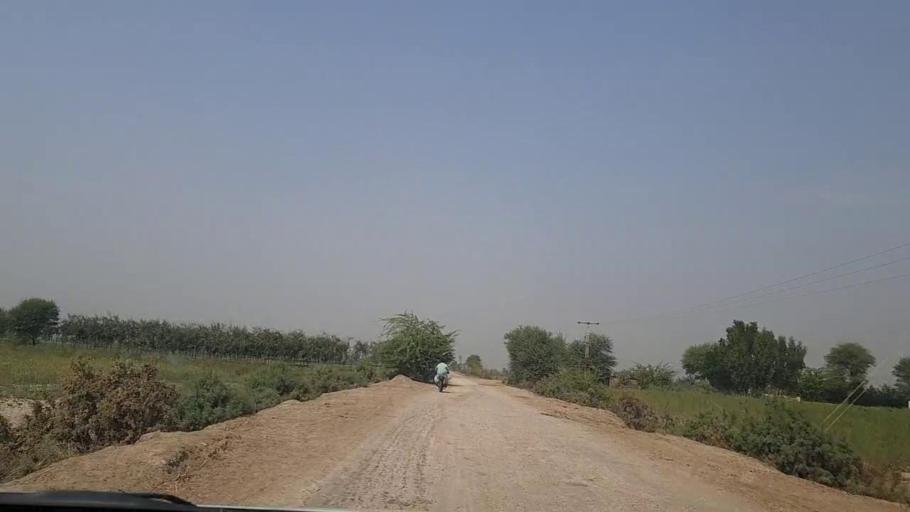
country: PK
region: Sindh
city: Mirpur Khas
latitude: 25.6084
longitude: 69.2010
